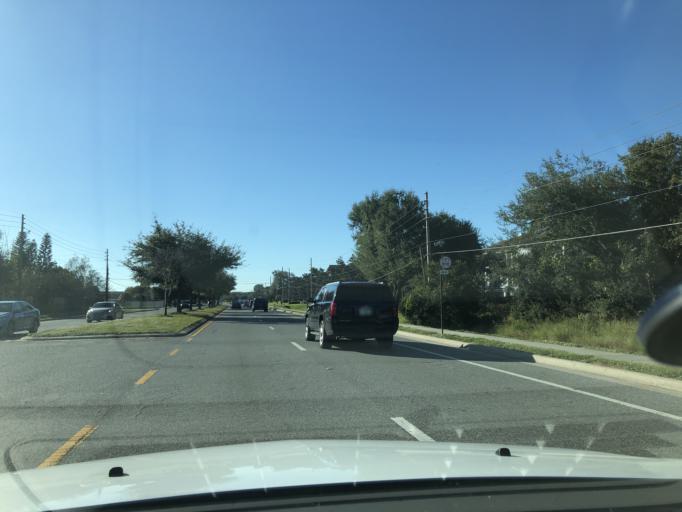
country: US
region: Florida
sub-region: Orange County
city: Oak Ridge
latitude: 28.4869
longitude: -81.4200
